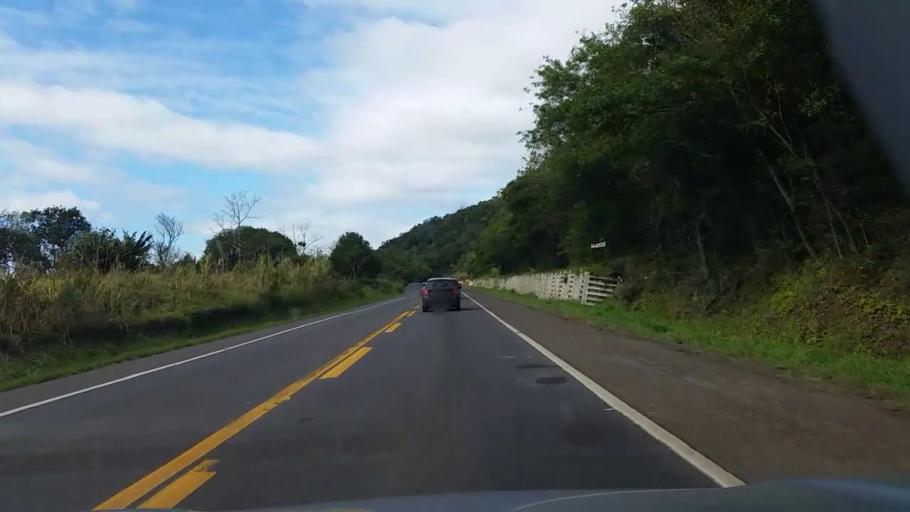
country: BR
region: Rio Grande do Sul
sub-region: Arroio Do Meio
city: Arroio do Meio
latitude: -29.3336
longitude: -52.0978
